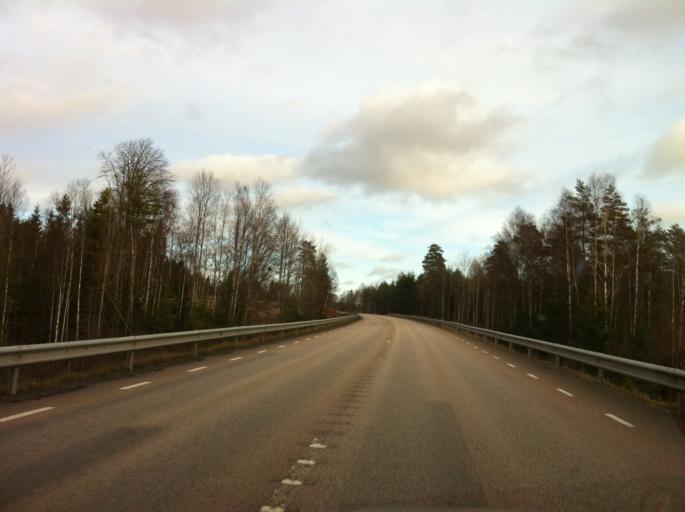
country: SE
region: Kronoberg
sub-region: Uppvidinge Kommun
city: Lenhovda
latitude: 57.1087
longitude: 15.2088
